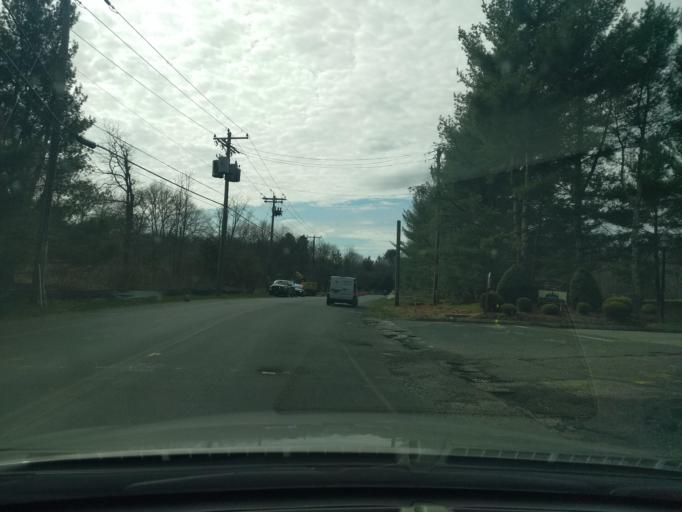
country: US
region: Connecticut
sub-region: Fairfield County
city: Newtown
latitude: 41.3411
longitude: -73.2470
